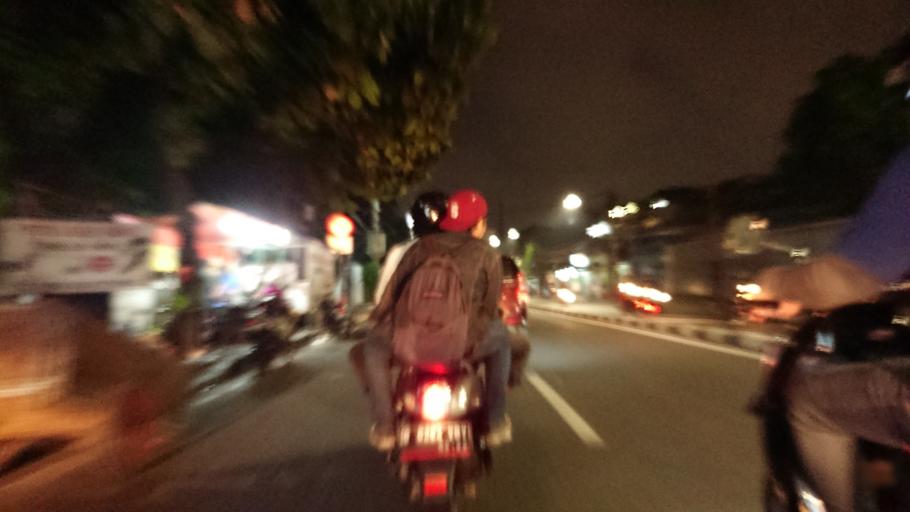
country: ID
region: Jakarta Raya
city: Jakarta
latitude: -6.1914
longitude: 106.8060
